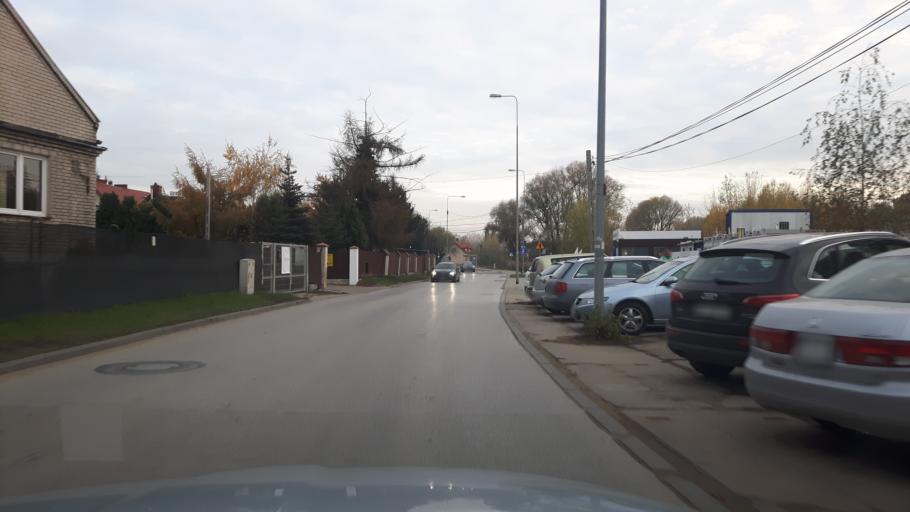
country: PL
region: Masovian Voivodeship
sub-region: Warszawa
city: Wilanow
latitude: 52.1806
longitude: 21.1005
